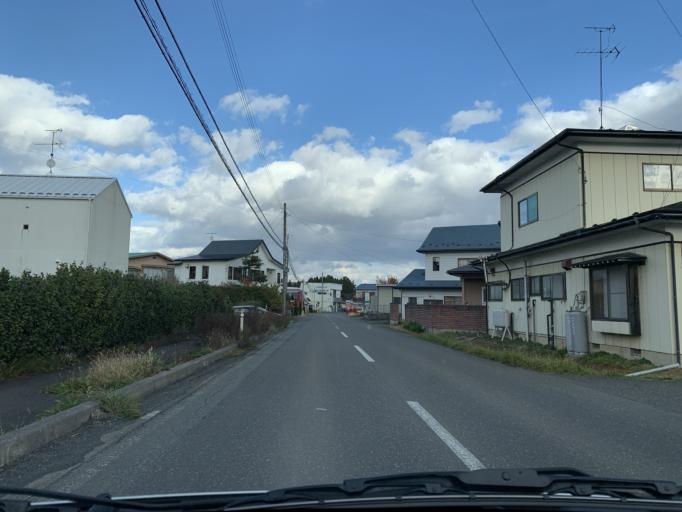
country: JP
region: Iwate
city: Mizusawa
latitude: 39.1322
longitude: 141.1092
